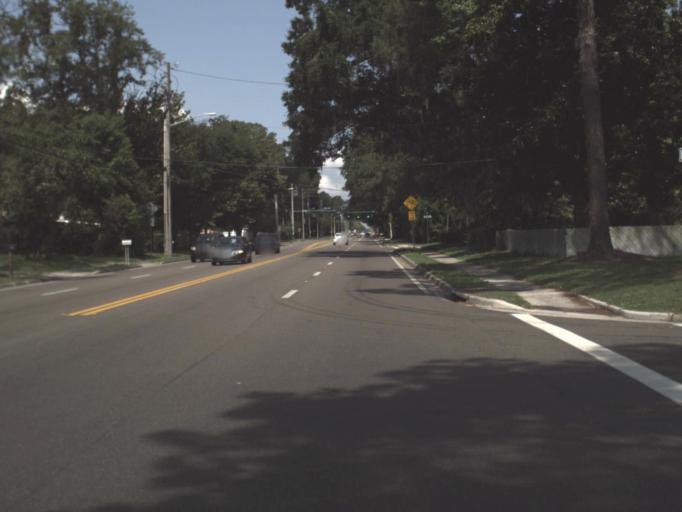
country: US
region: Florida
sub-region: Alachua County
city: Gainesville
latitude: 29.6739
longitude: -82.3121
